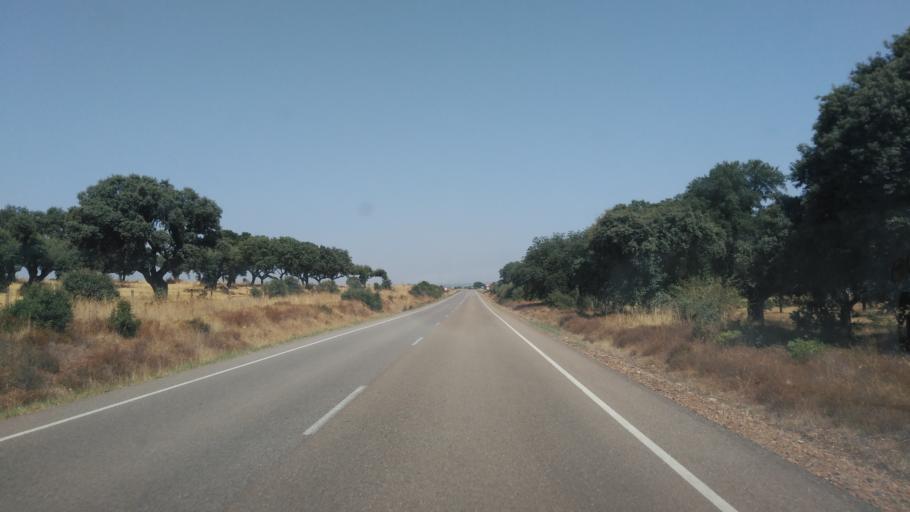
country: ES
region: Castille and Leon
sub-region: Provincia de Salamanca
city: Abusejo
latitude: 40.6909
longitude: -6.1323
